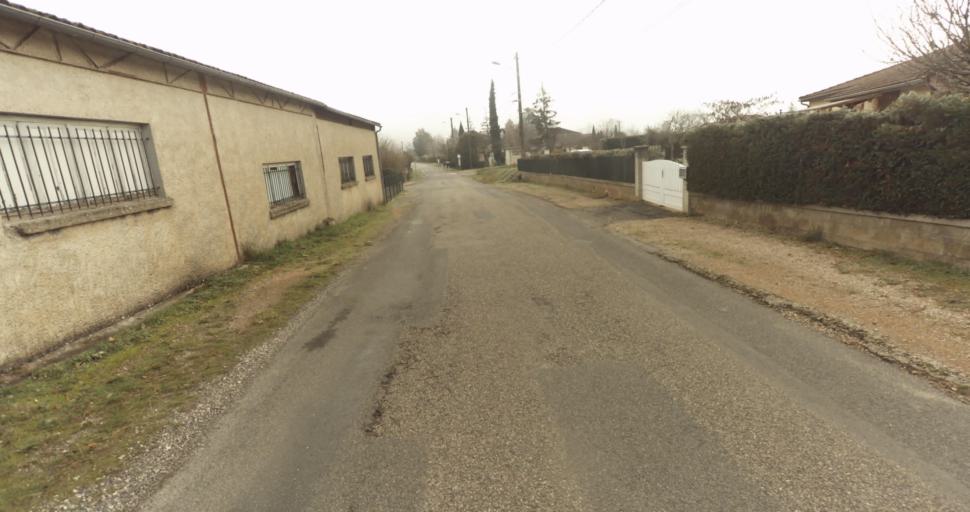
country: FR
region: Midi-Pyrenees
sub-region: Departement du Lot
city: Figeac
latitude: 44.6229
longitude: 2.0226
